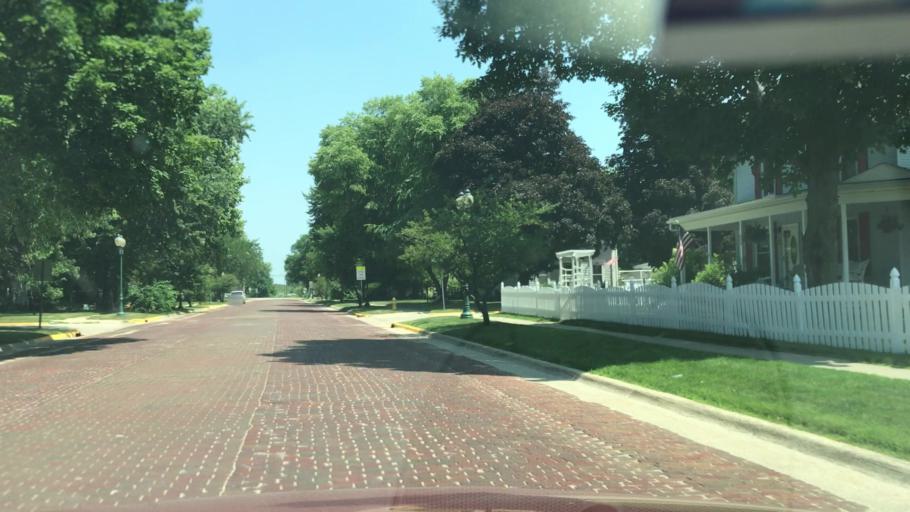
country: US
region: Illinois
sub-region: Winnebago County
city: Cherry Valley
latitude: 42.2348
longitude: -88.9504
